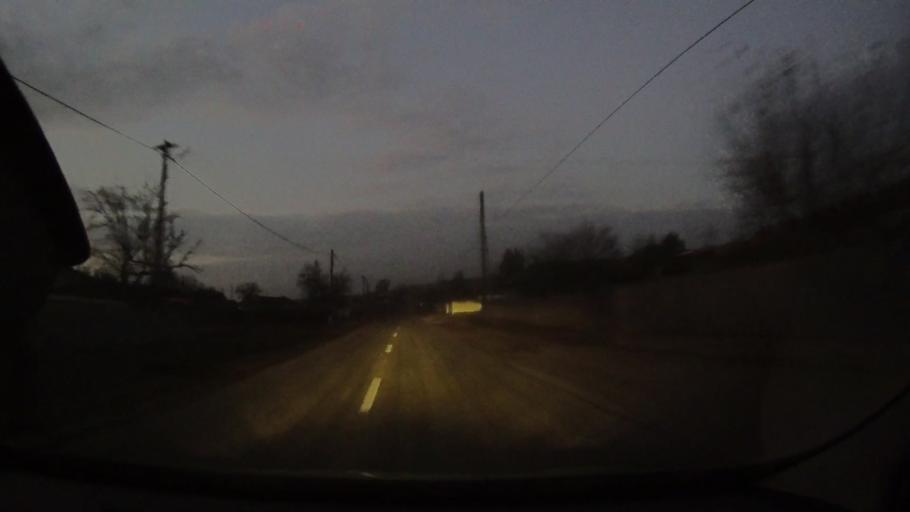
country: RO
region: Constanta
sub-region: Comuna Aliman
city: Aliman
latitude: 44.1450
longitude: 27.8333
